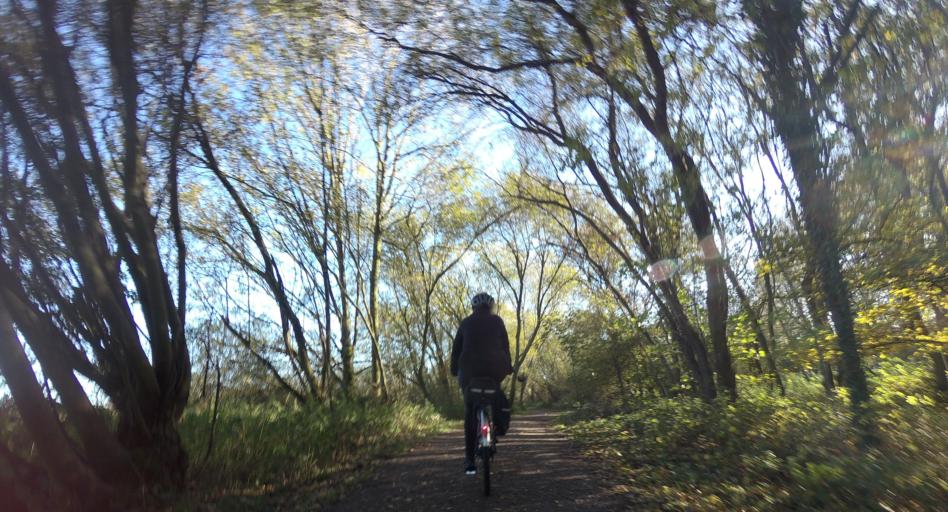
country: GB
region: England
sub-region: West Sussex
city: Steyning
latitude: 50.8796
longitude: -0.3124
